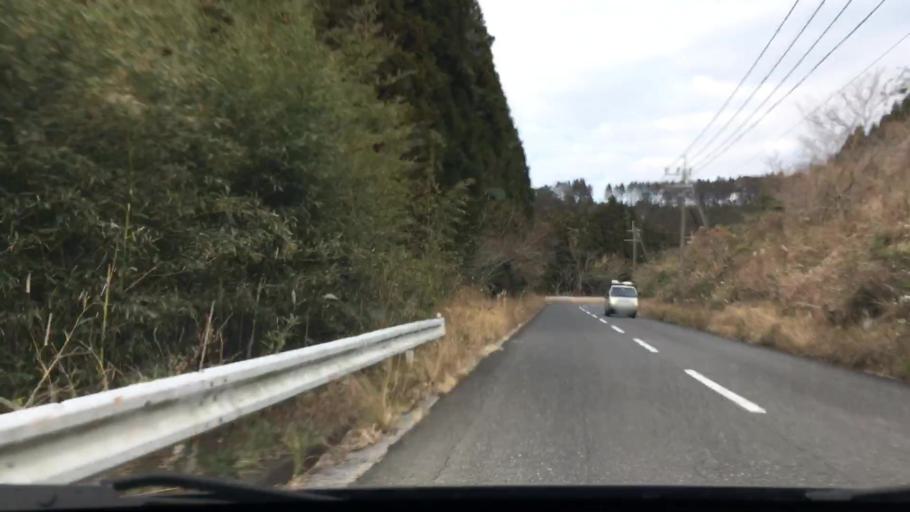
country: JP
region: Miyazaki
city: Nichinan
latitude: 31.6655
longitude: 131.3178
